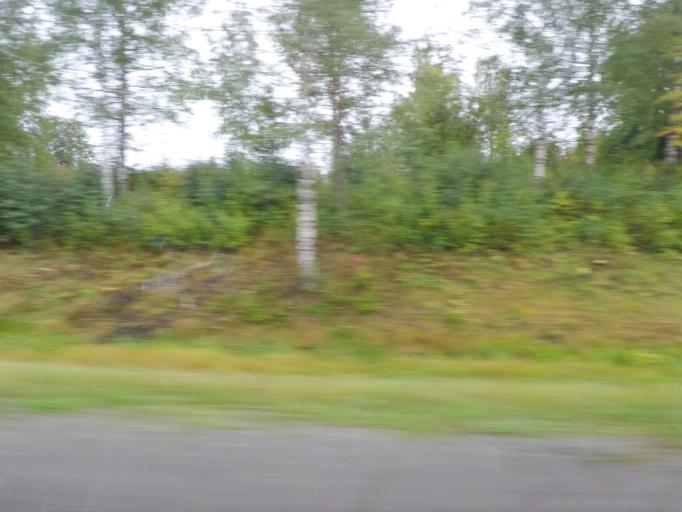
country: FI
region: Northern Savo
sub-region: Kuopio
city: Kuopio
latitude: 62.9023
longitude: 27.6799
